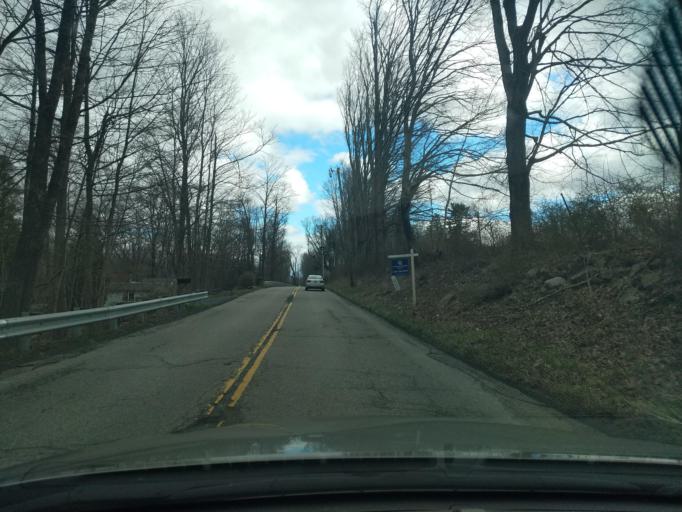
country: US
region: Connecticut
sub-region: Fairfield County
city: Newtown
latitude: 41.3644
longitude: -73.3288
